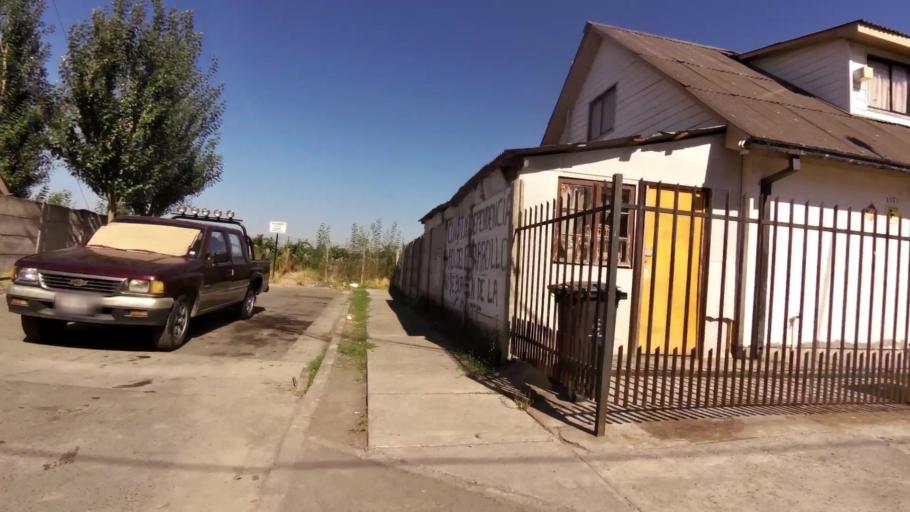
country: CL
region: Maule
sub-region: Provincia de Curico
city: Curico
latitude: -34.9781
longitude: -71.2672
